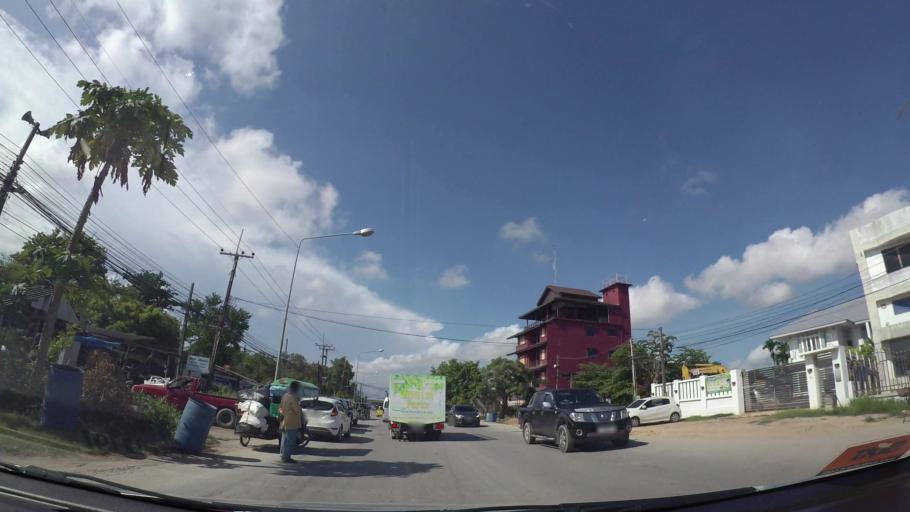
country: TH
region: Rayong
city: Rayong
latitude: 12.6810
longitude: 101.2967
